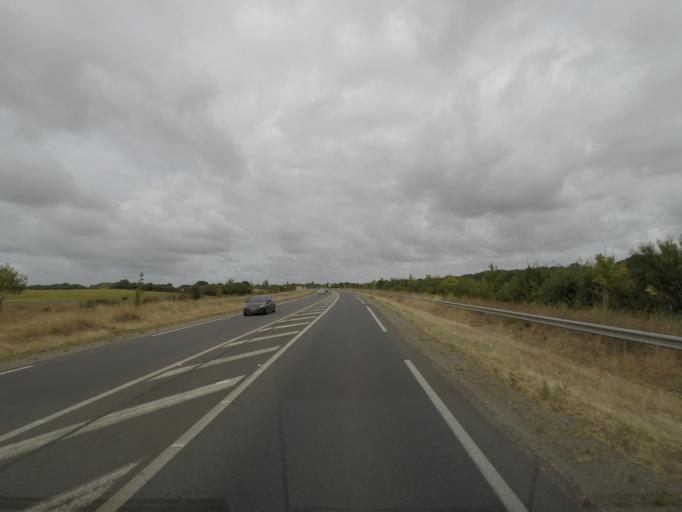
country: FR
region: Poitou-Charentes
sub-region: Departement des Deux-Sevres
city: Thorigne
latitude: 46.2852
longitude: -0.2657
